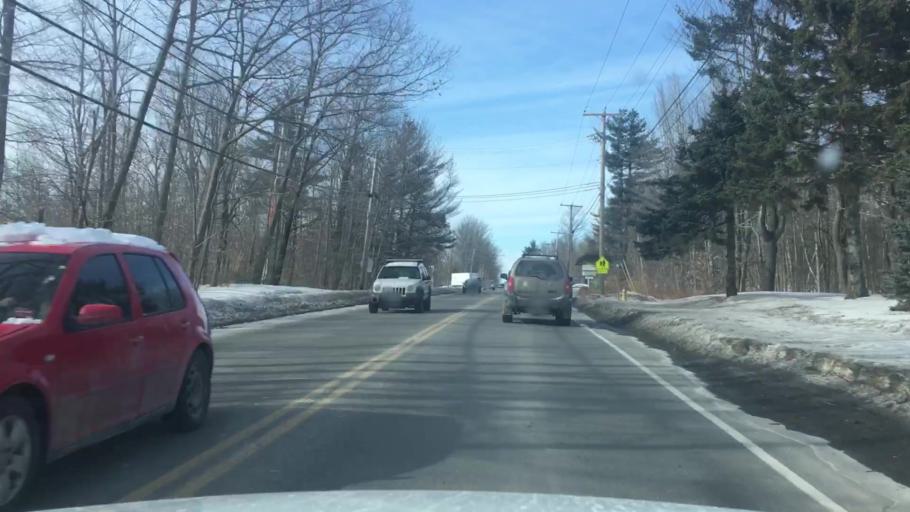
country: US
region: Maine
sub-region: Penobscot County
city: Bangor
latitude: 44.8299
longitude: -68.7854
